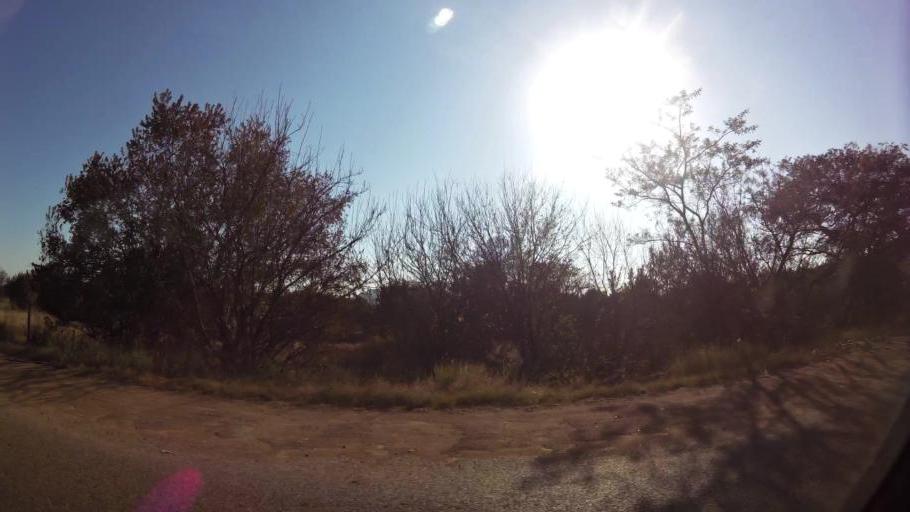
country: ZA
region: Gauteng
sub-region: City of Tshwane Metropolitan Municipality
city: Pretoria
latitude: -25.6514
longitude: 28.1619
